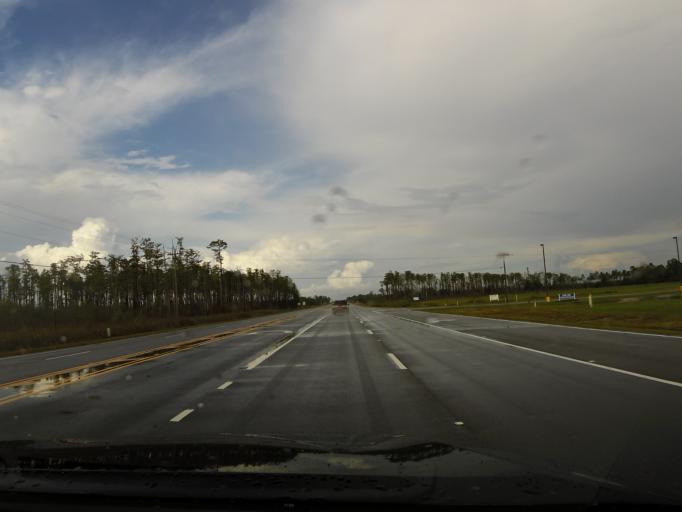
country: US
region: Georgia
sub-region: Long County
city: Ludowici
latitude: 31.7233
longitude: -81.7262
